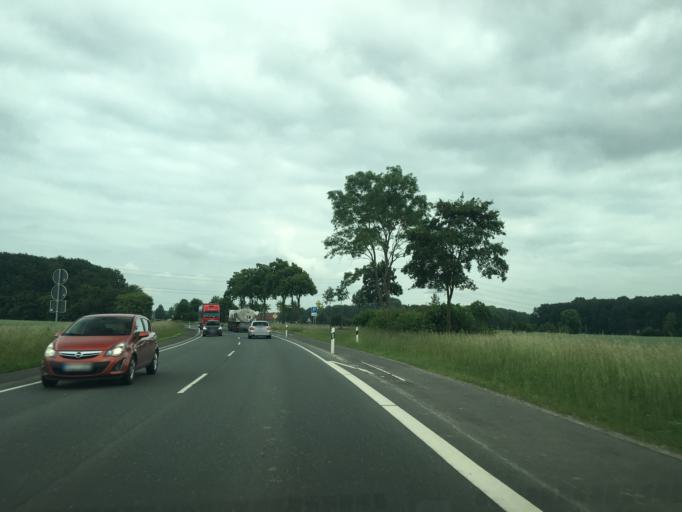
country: DE
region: North Rhine-Westphalia
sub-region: Regierungsbezirk Munster
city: Laer
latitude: 52.0508
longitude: 7.4094
